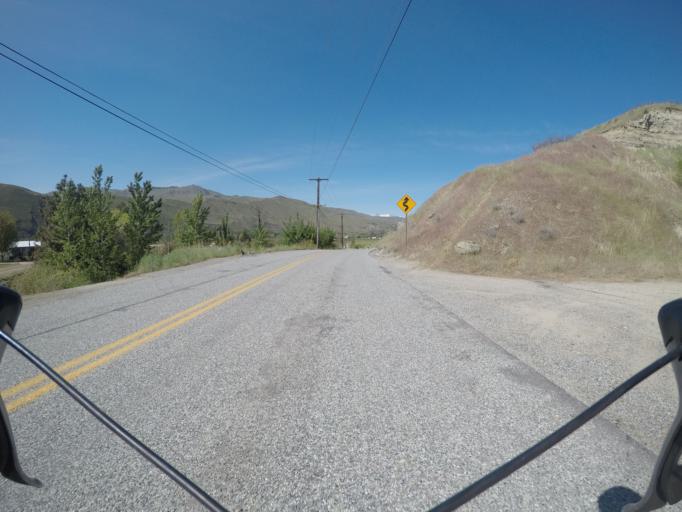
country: US
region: Washington
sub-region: Chelan County
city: Sunnyslope
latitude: 47.4693
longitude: -120.3486
